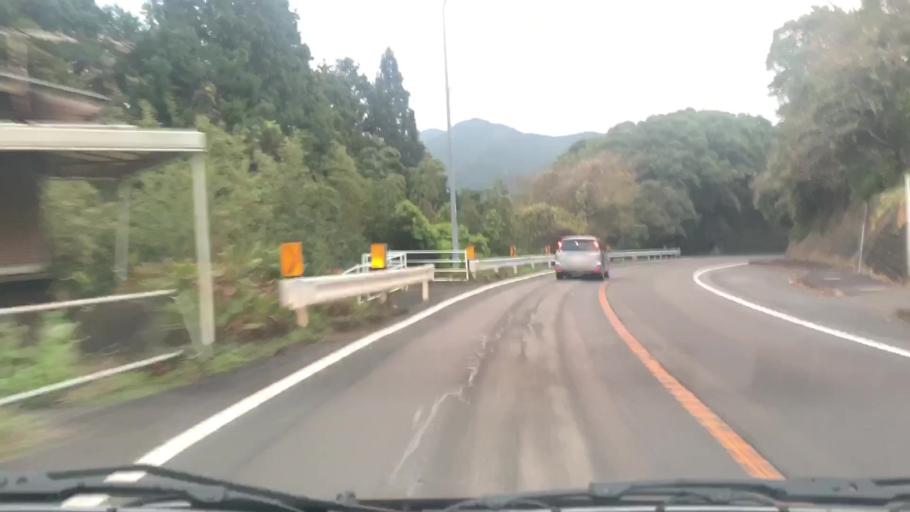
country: JP
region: Saga Prefecture
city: Ureshinomachi-shimojuku
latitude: 33.0580
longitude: 129.9492
